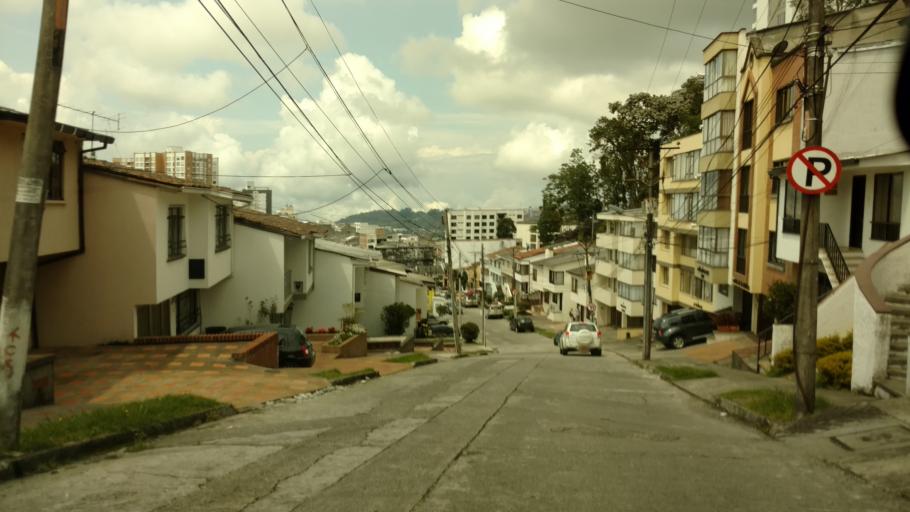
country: CO
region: Caldas
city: Villamaria
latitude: 5.0501
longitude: -75.4848
